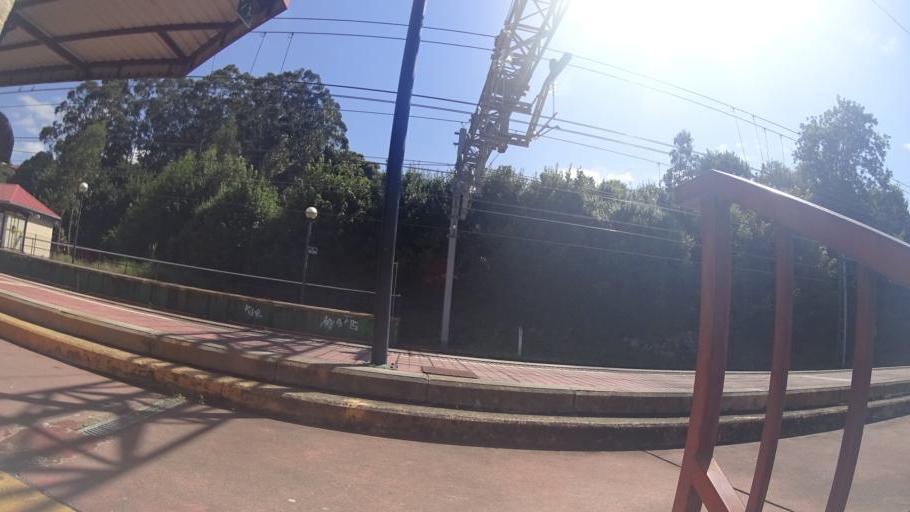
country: ES
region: Asturias
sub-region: Province of Asturias
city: Ribadesella
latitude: 43.4594
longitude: -5.0549
